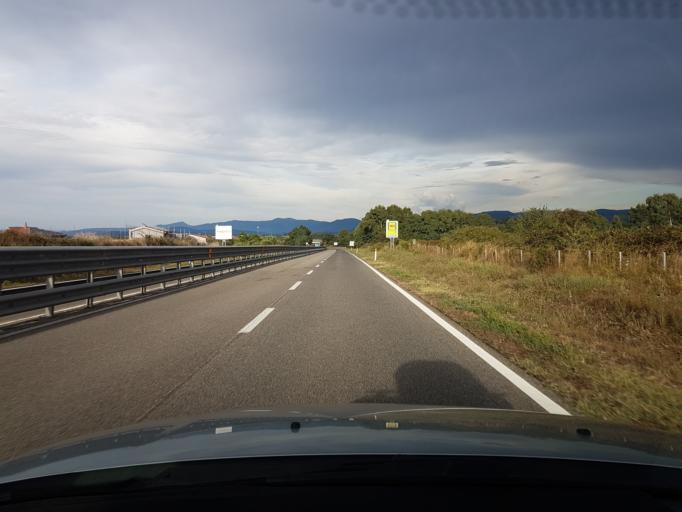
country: IT
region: Sardinia
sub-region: Provincia di Oristano
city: Ghilarza
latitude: 40.1156
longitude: 8.8325
